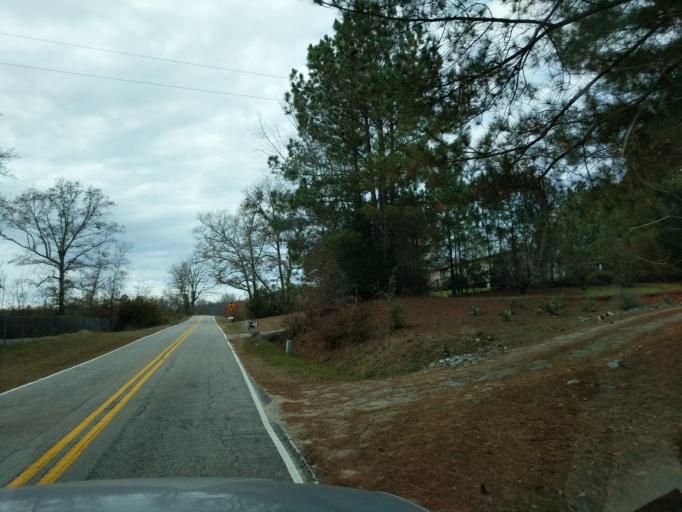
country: US
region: South Carolina
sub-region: Pickens County
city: Arial
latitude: 34.8869
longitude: -82.6451
